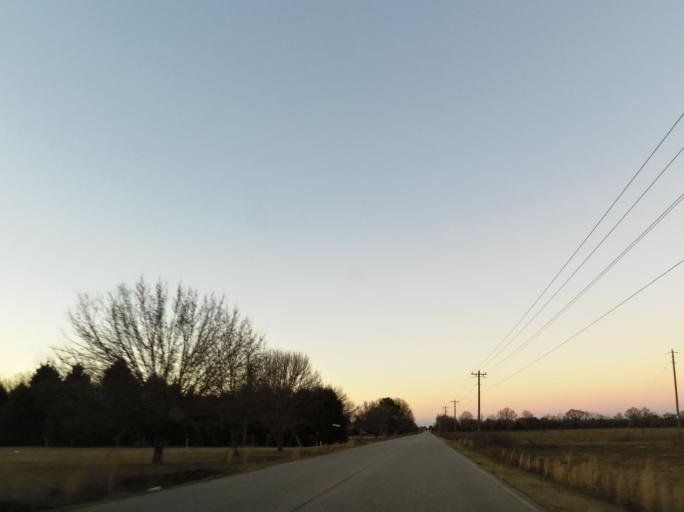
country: US
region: Georgia
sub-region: Peach County
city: Byron
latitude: 32.5998
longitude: -83.7481
